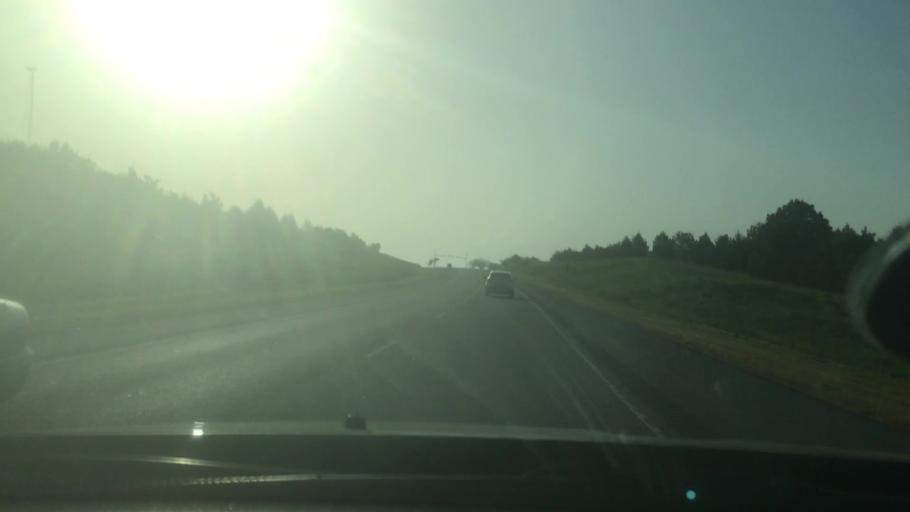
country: US
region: Oklahoma
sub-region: Coal County
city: Coalgate
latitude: 34.6113
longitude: -96.4296
